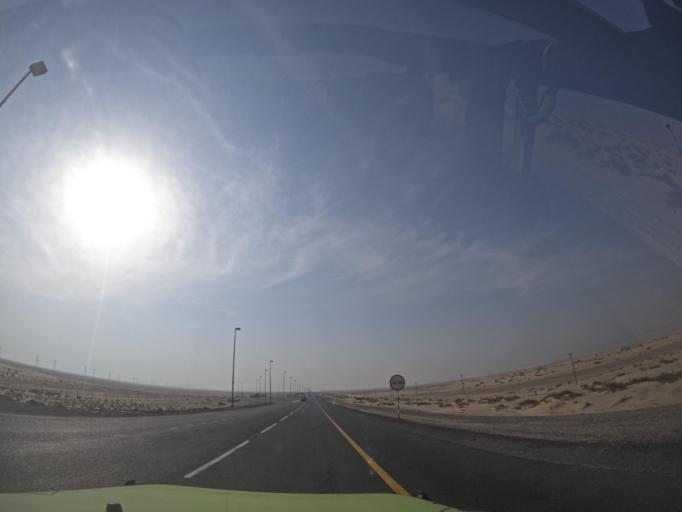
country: AE
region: Dubai
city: Dubai
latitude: 24.7685
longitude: 55.0928
